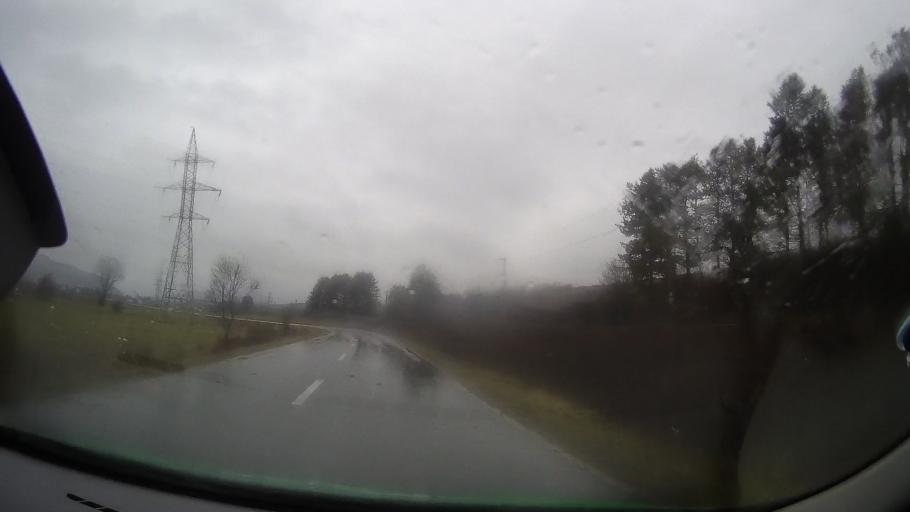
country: RO
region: Bistrita-Nasaud
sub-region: Comuna Mariselu
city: Mariselu
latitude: 47.0282
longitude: 24.4946
